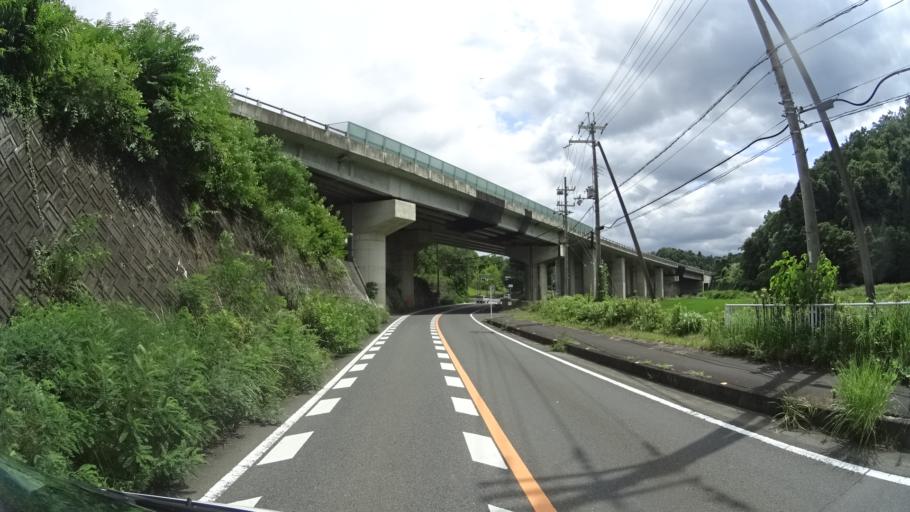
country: JP
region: Kyoto
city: Ayabe
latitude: 35.3308
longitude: 135.2679
